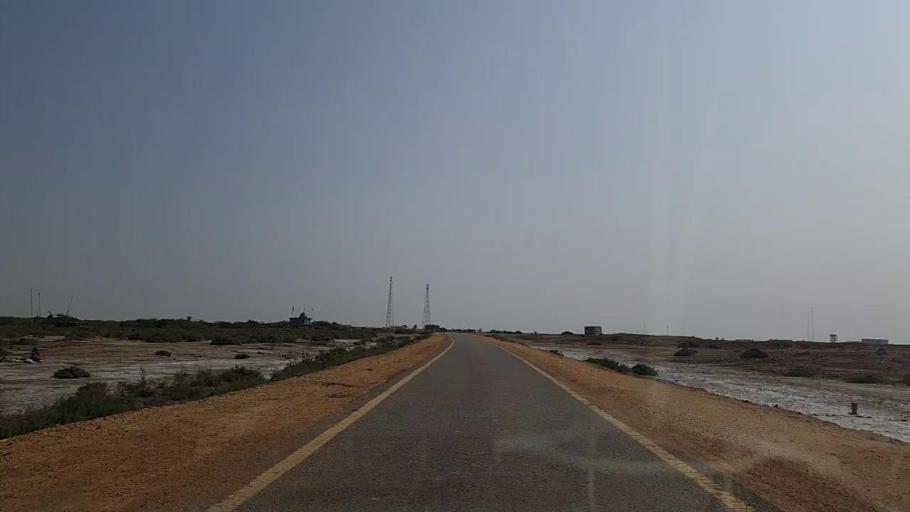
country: PK
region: Sindh
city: Chuhar Jamali
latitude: 24.1690
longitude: 67.8953
